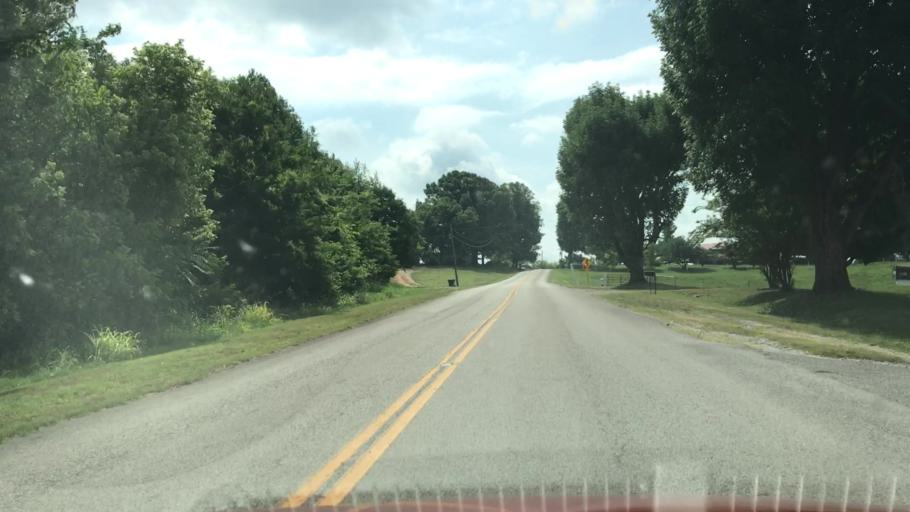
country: US
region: Kentucky
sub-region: Barren County
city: Glasgow
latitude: 36.9768
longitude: -85.8976
